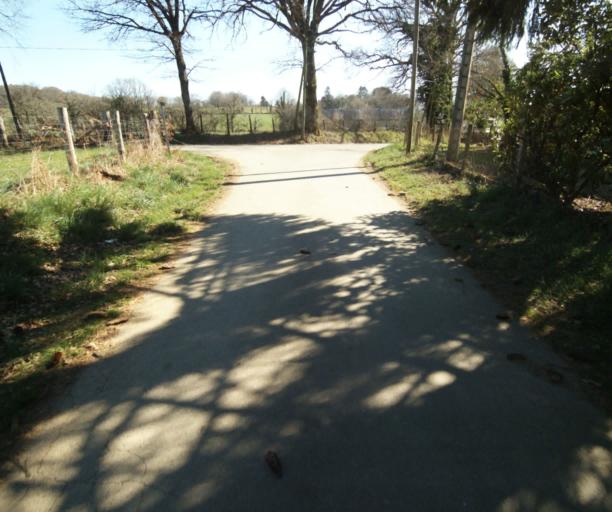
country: FR
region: Limousin
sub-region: Departement de la Correze
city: Chamboulive
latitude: 45.4774
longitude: 1.7363
